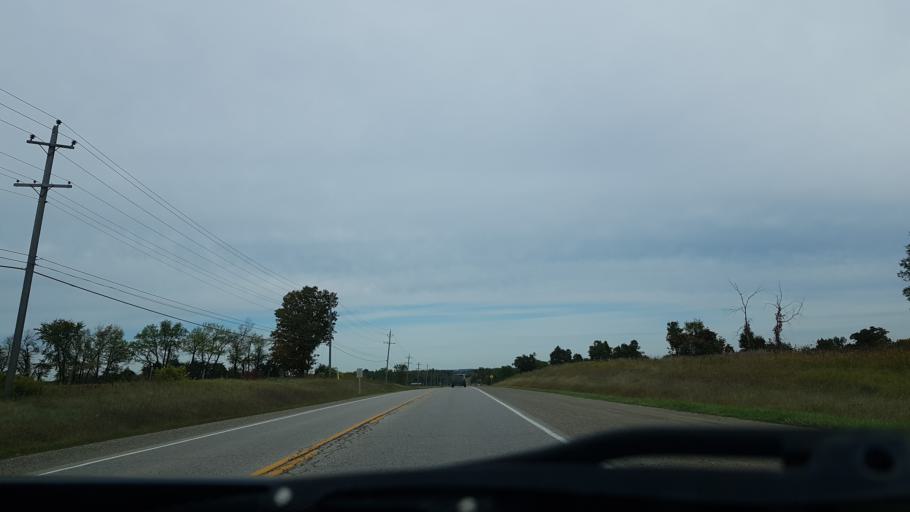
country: CA
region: Ontario
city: Orangeville
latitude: 43.7885
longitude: -80.0749
